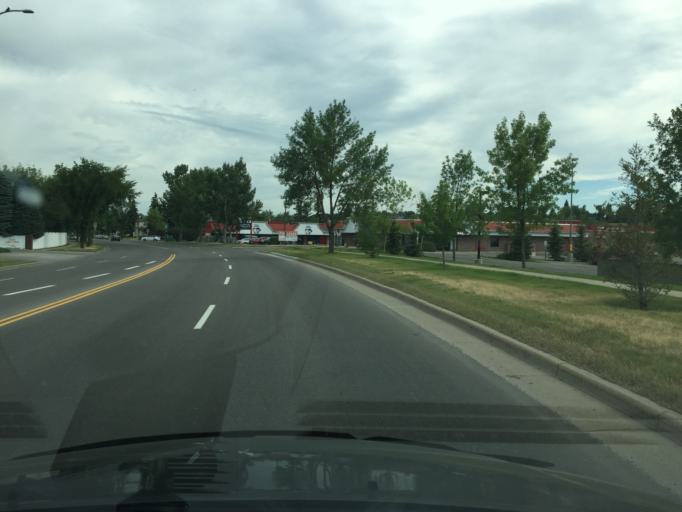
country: CA
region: Alberta
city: Calgary
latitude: 50.9295
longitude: -114.0274
